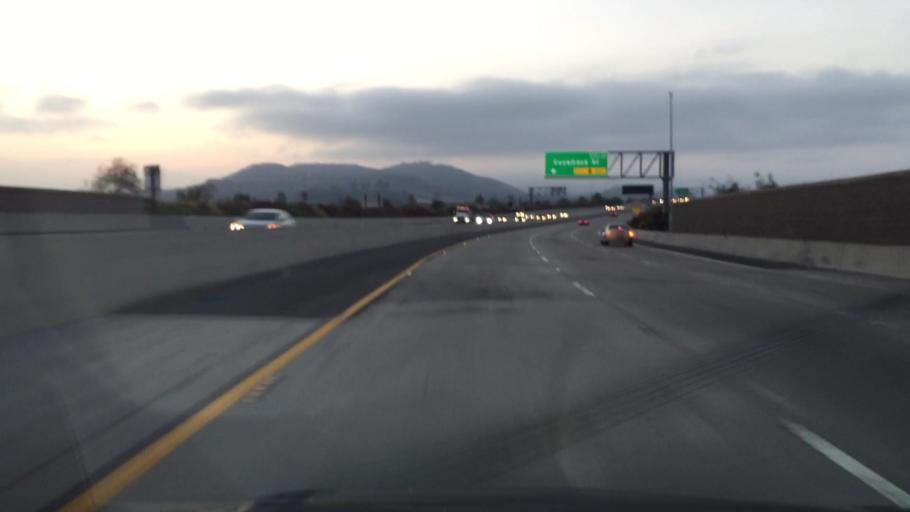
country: US
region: California
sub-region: San Diego County
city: Santee
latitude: 32.8364
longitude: -116.9931
